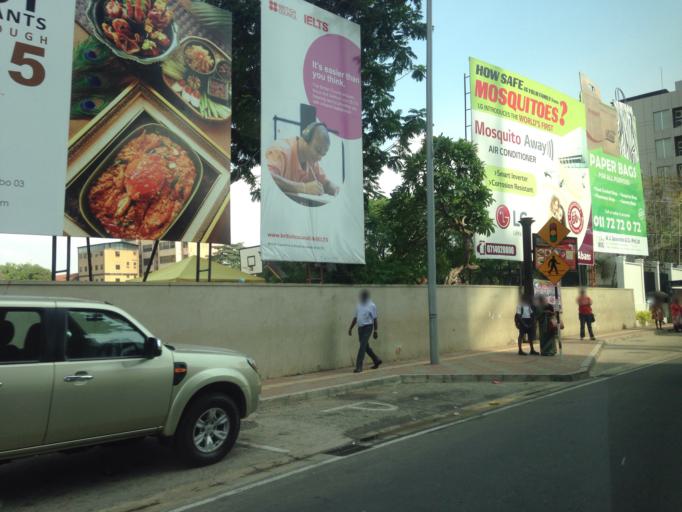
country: LK
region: Western
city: Colombo
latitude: 6.9061
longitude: 79.8535
